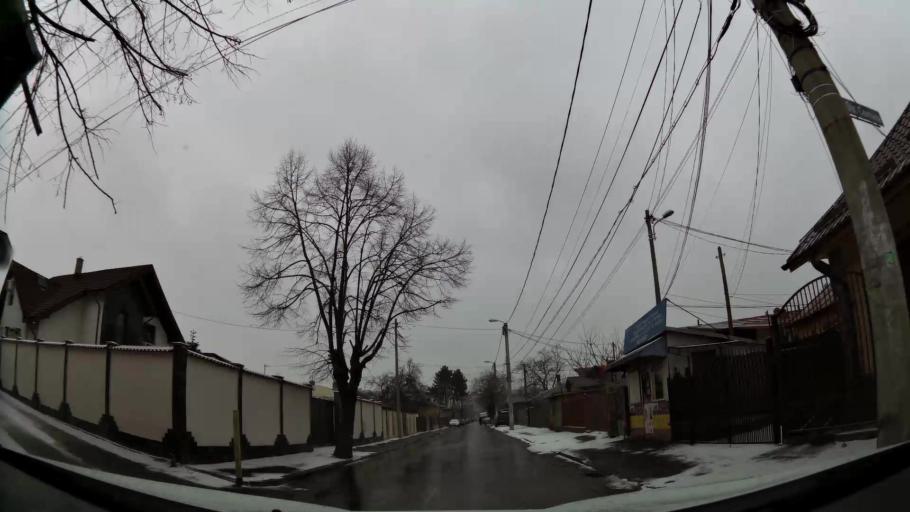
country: RO
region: Prahova
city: Ploiesti
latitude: 44.9459
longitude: 26.0014
